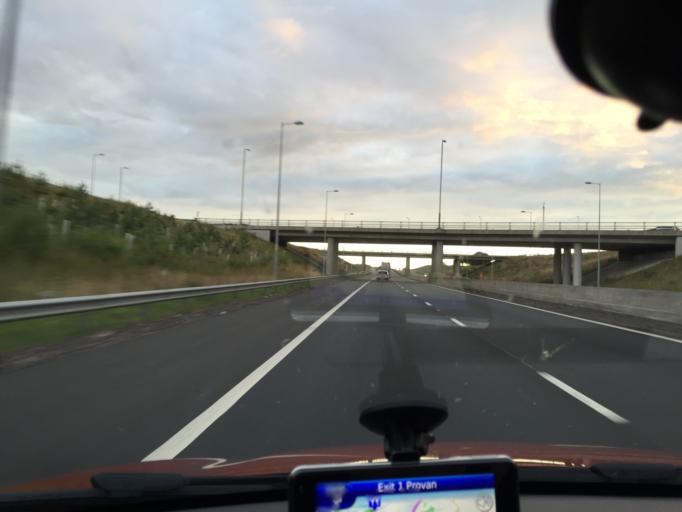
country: GB
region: Scotland
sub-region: North Lanarkshire
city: Stepps
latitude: 55.9026
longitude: -4.1363
